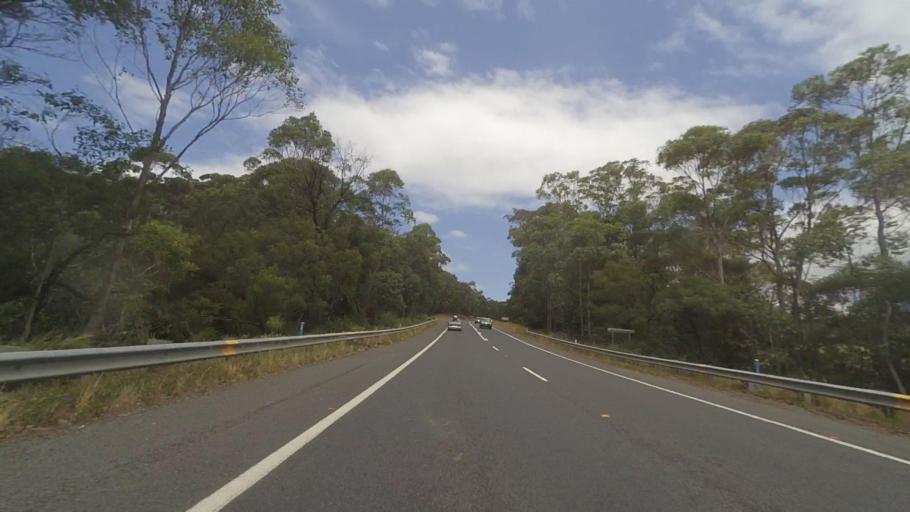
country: AU
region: New South Wales
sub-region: Shoalhaven Shire
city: Milton
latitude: -35.2278
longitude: 150.4352
